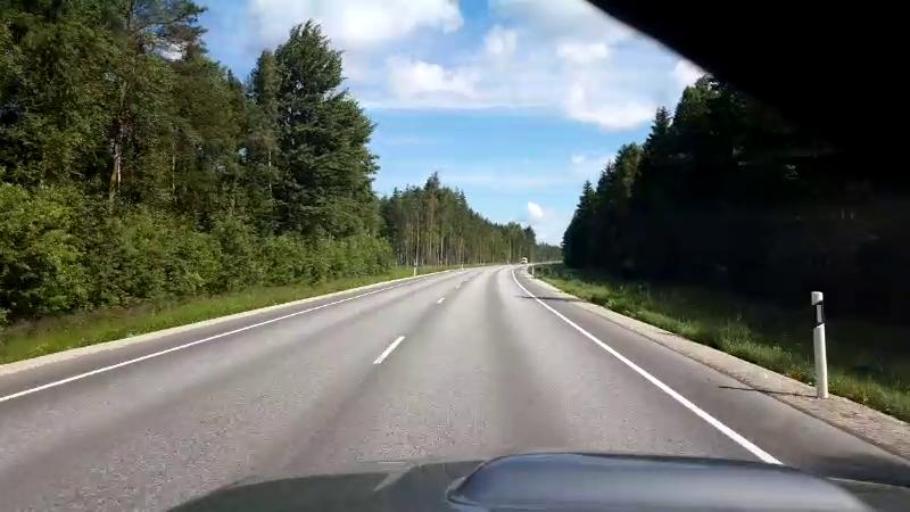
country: EE
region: Jaervamaa
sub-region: Paide linn
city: Paide
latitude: 58.9999
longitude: 25.6778
